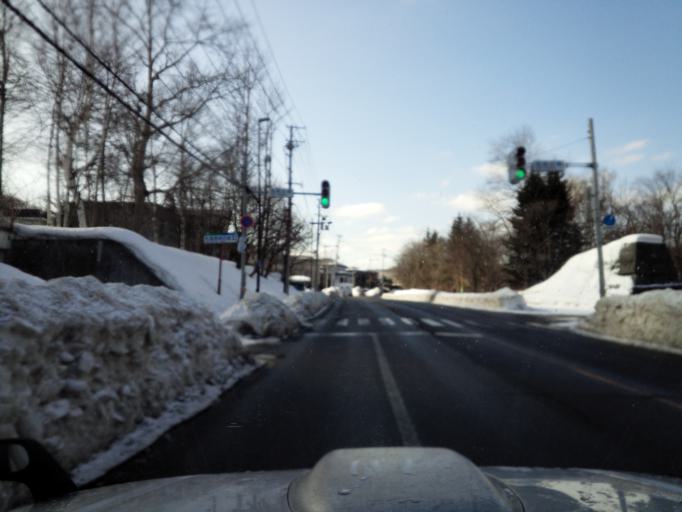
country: JP
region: Hokkaido
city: Sapporo
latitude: 42.9407
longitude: 141.3447
